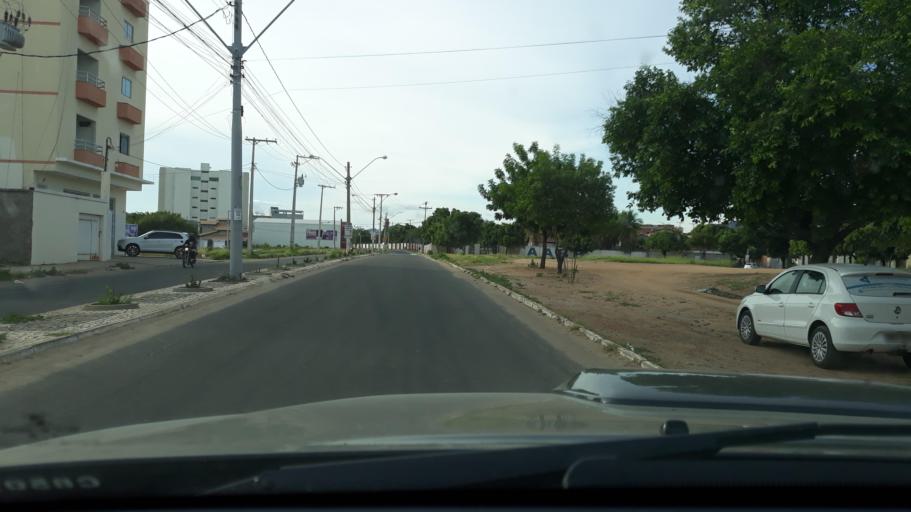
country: BR
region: Bahia
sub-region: Guanambi
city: Guanambi
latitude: -14.2331
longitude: -42.7757
